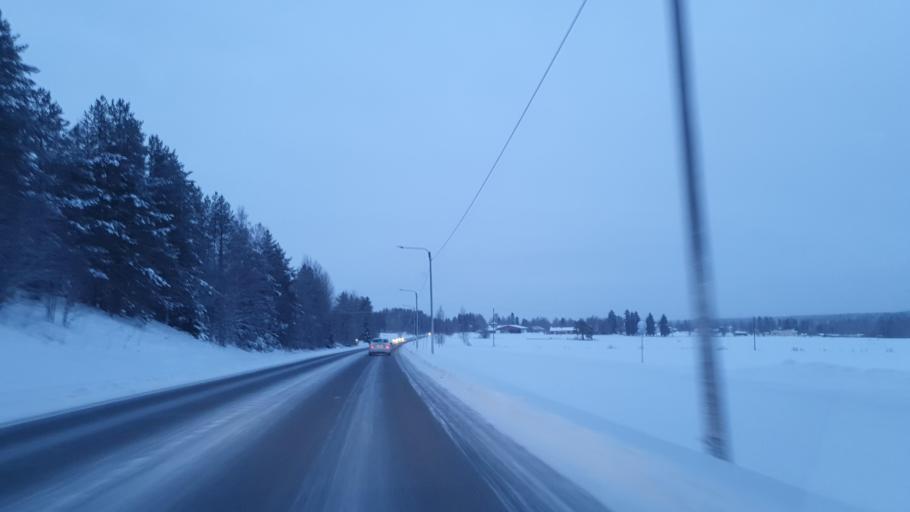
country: FI
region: Northern Ostrobothnia
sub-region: Oulu
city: Muhos
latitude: 64.8389
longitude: 25.9067
